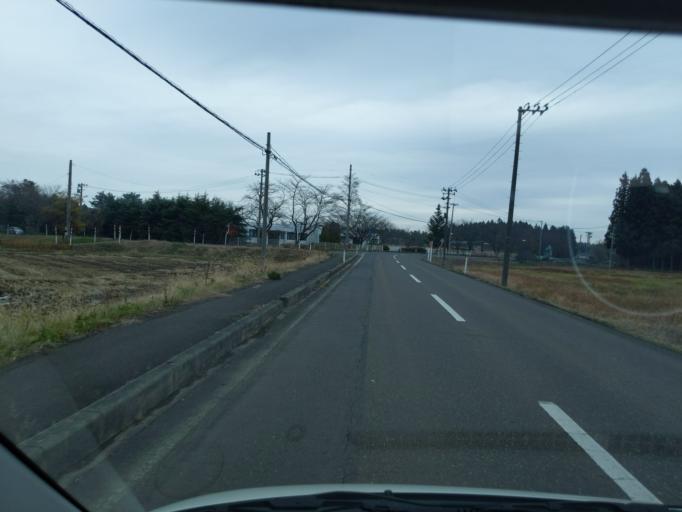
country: JP
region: Iwate
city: Mizusawa
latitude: 39.1050
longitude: 141.0971
